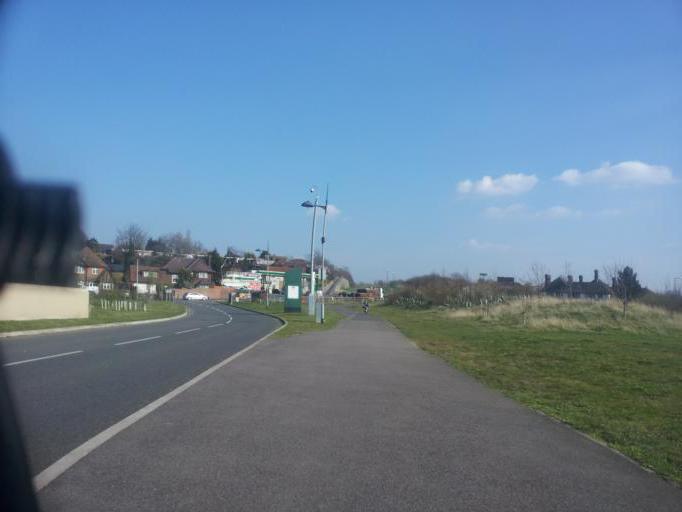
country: GB
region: England
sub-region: Kent
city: Gravesend
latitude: 51.4178
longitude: 0.3589
